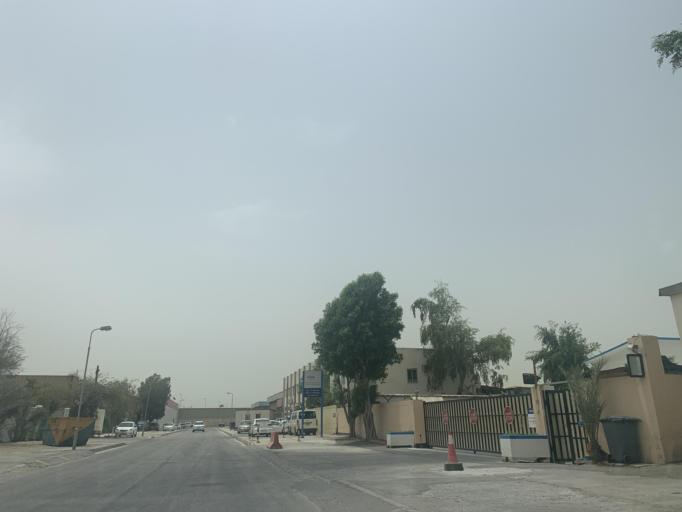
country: BH
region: Northern
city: Sitrah
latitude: 26.1792
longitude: 50.6075
